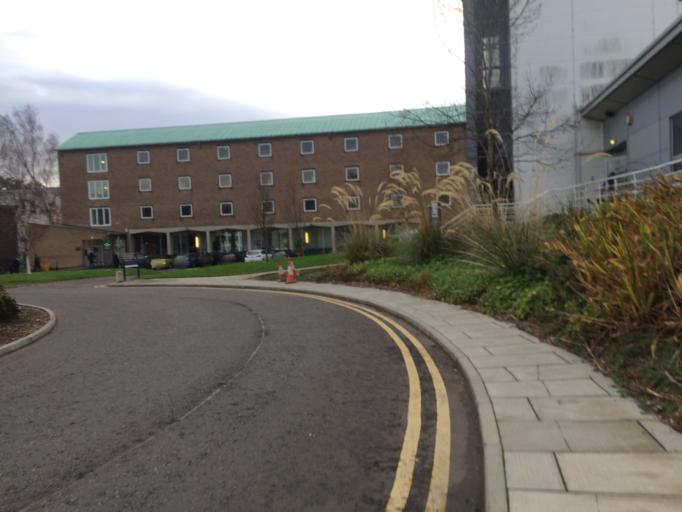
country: GB
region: Scotland
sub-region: Edinburgh
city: Edinburgh
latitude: 55.9224
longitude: -3.1775
